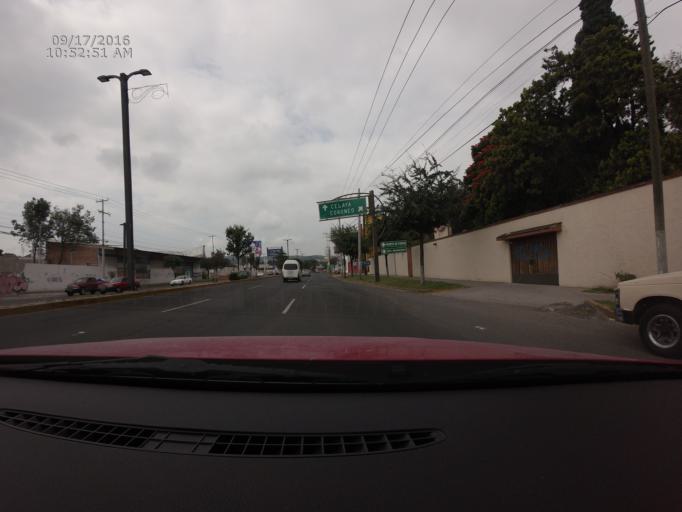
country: MX
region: Queretaro
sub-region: Corregidora
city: El Pueblito
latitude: 20.5351
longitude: -100.4370
